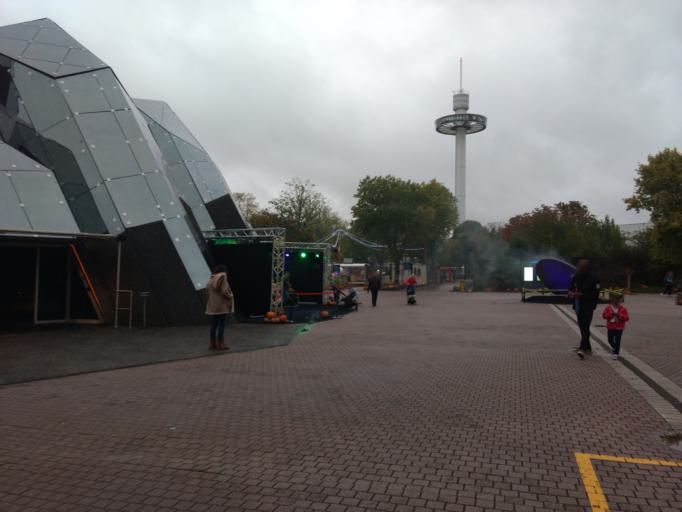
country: FR
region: Poitou-Charentes
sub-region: Departement de la Vienne
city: Jaunay-Clan
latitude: 46.6704
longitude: 0.3699
